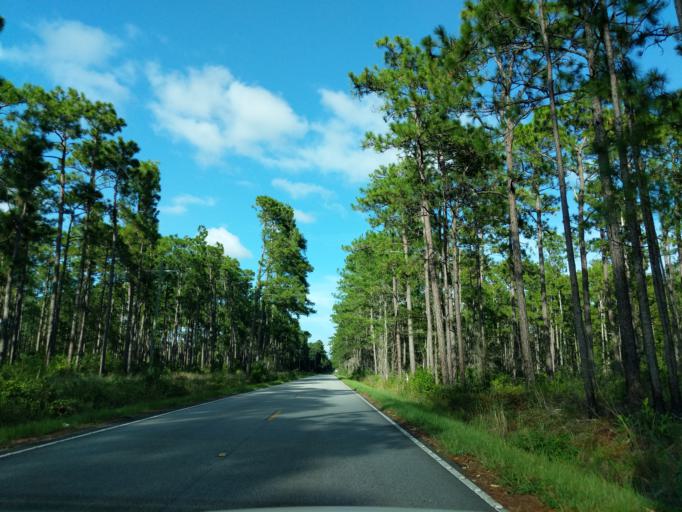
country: US
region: South Carolina
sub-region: Charleston County
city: Awendaw
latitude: 33.1369
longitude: -79.4309
